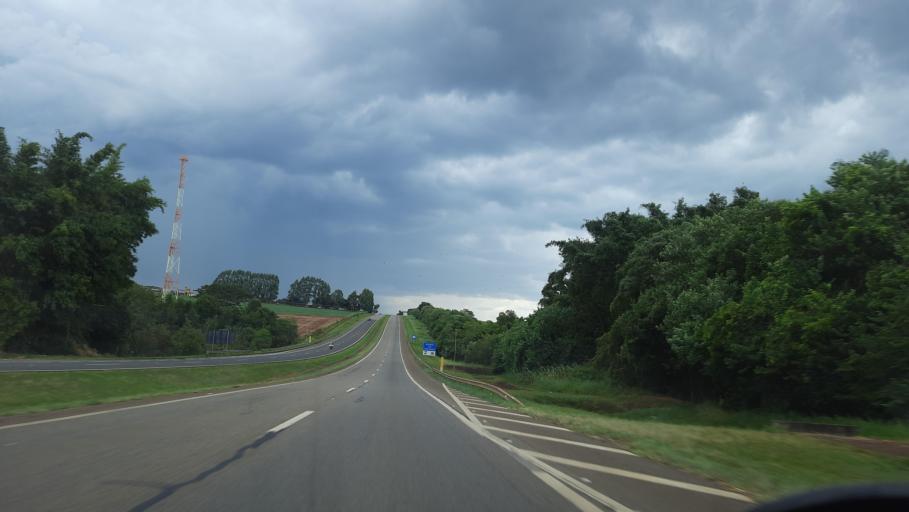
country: BR
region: Sao Paulo
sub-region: Aguai
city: Aguai
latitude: -22.0480
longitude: -47.0301
